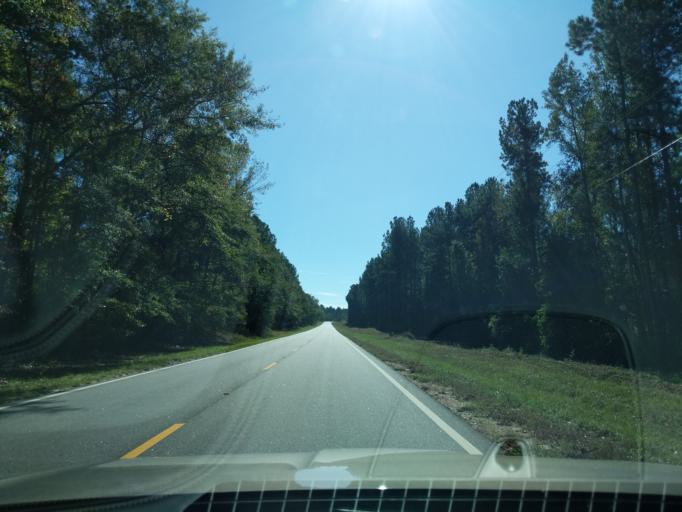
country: US
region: Georgia
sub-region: Richmond County
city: Hephzibah
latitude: 33.2839
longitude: -82.0196
